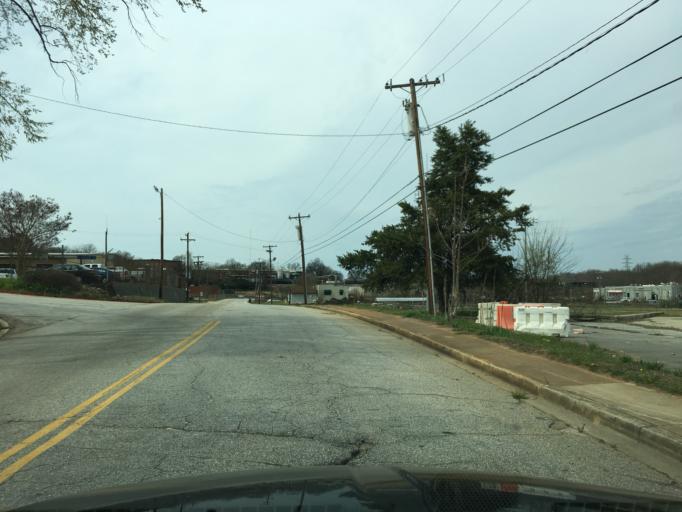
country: US
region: South Carolina
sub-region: Greenville County
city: Greenville
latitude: 34.8505
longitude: -82.4139
